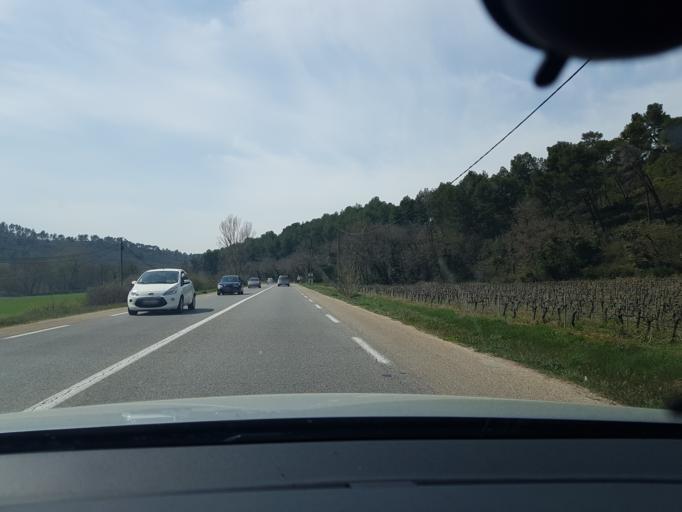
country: FR
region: Provence-Alpes-Cote d'Azur
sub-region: Departement des Bouches-du-Rhone
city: Gardanne
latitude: 43.4714
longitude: 5.4577
